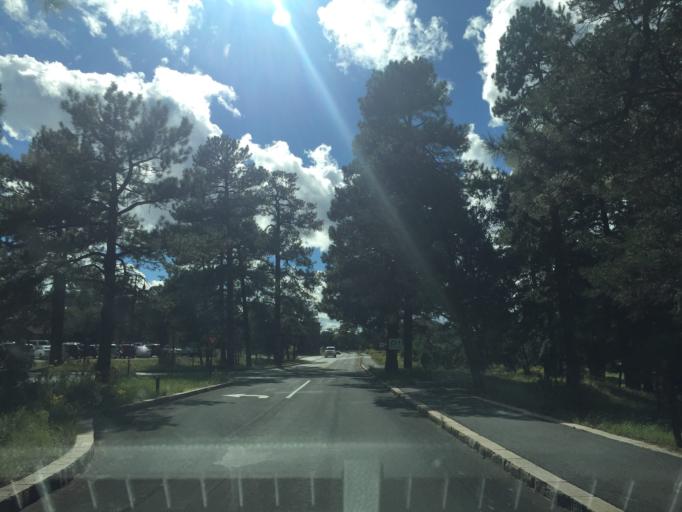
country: US
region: Arizona
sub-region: Coconino County
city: Grand Canyon
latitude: 36.0557
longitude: -112.1378
